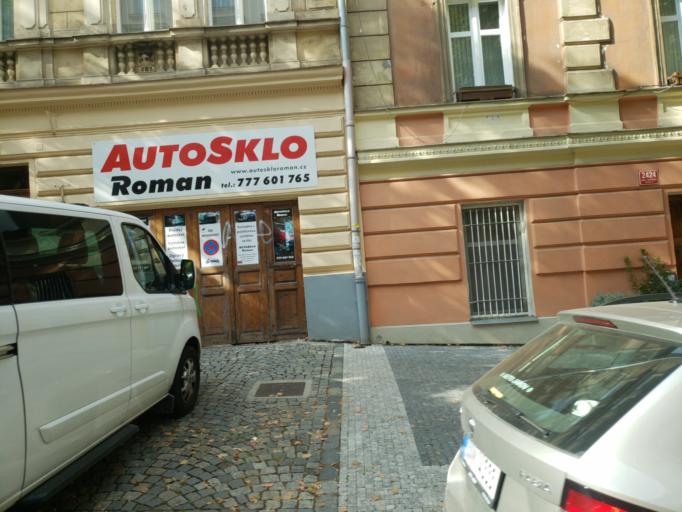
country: CZ
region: Praha
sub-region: Praha 8
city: Karlin
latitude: 50.0802
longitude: 14.4546
